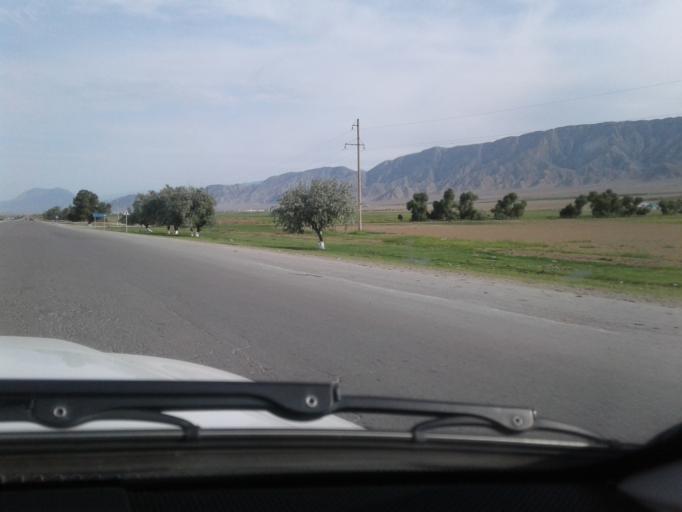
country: TM
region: Ahal
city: Arcabil
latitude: 38.2069
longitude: 57.8184
